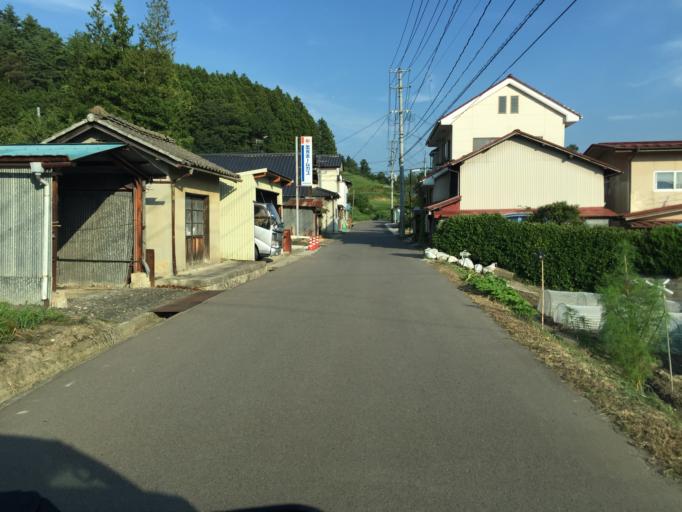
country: JP
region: Fukushima
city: Fukushima-shi
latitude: 37.6707
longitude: 140.5719
